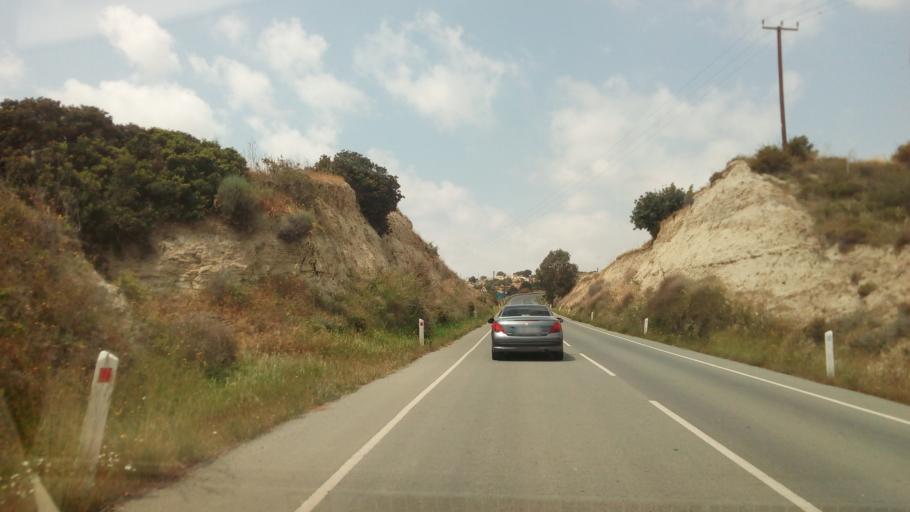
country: CY
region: Limassol
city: Pissouri
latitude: 34.6773
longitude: 32.7208
